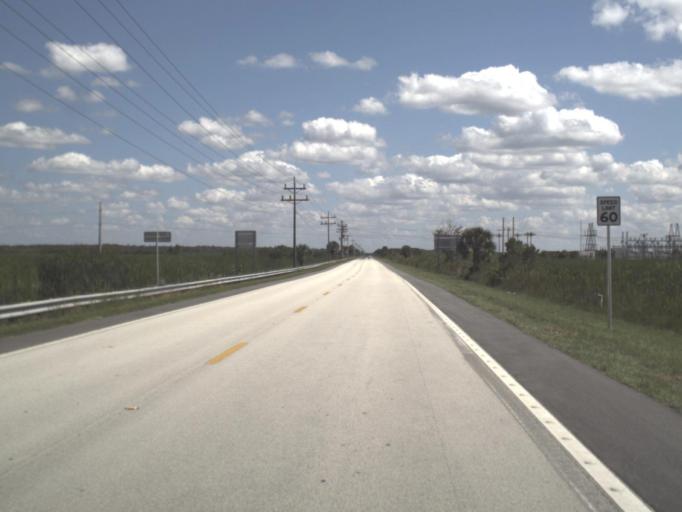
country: US
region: Florida
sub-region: Collier County
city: Marco
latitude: 25.9099
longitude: -81.3622
